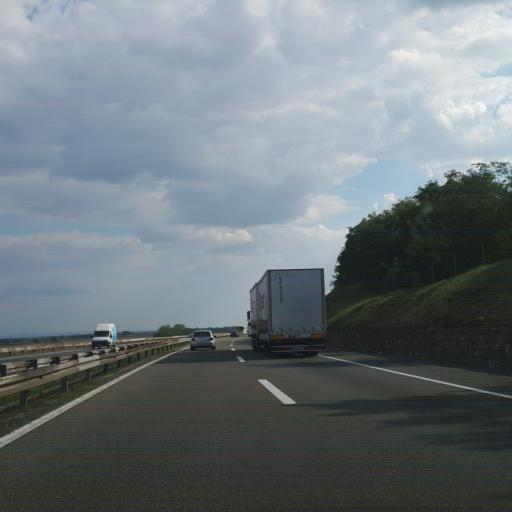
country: RS
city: Lugavcina
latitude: 44.5264
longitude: 21.0079
